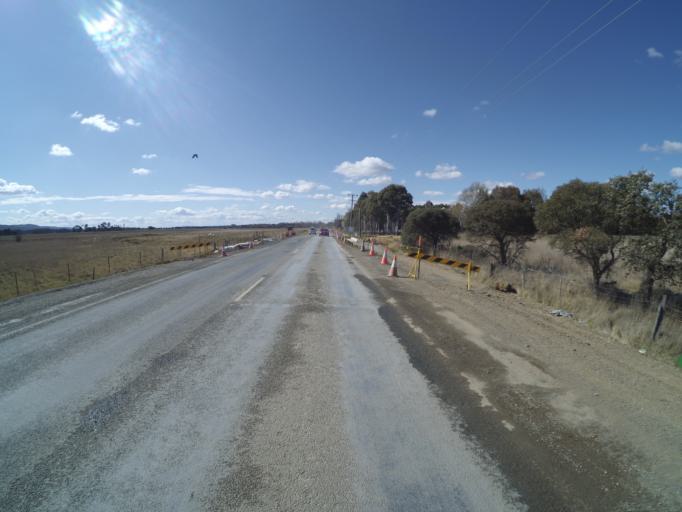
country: AU
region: New South Wales
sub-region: Palerang
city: Bungendore
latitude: -35.2648
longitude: 149.4329
